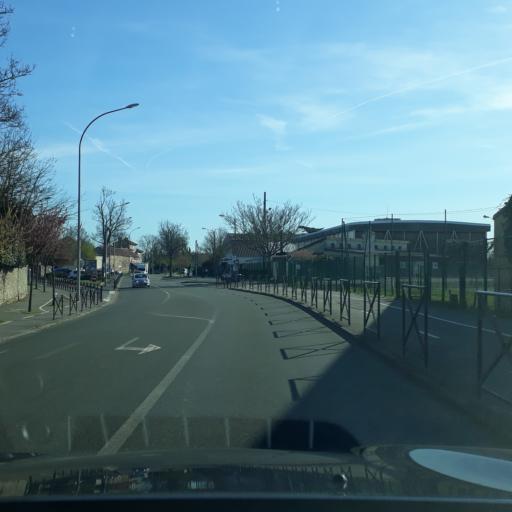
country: FR
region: Ile-de-France
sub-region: Departement de l'Essonne
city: Mennecy
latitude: 48.5638
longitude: 2.4339
